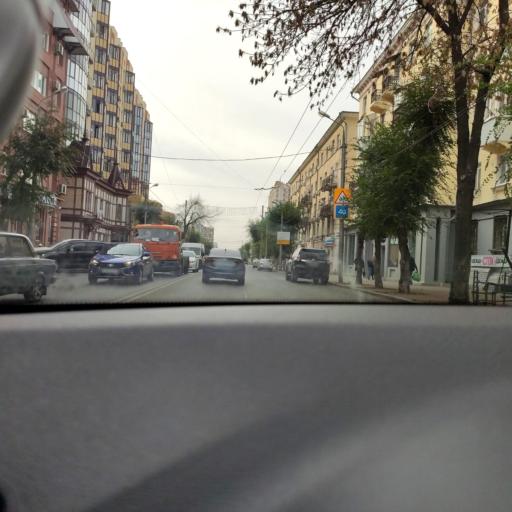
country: RU
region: Samara
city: Samara
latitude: 53.1961
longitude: 50.1076
